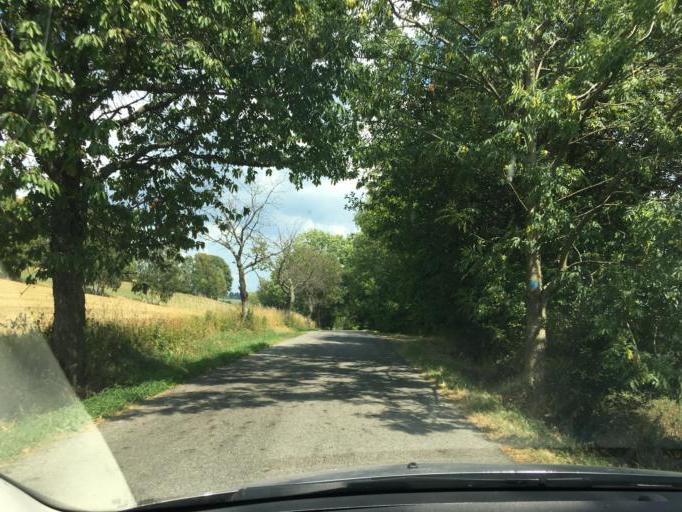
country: CZ
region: Liberecky
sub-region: Okres Semily
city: Ponikla
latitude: 50.6736
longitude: 15.4822
